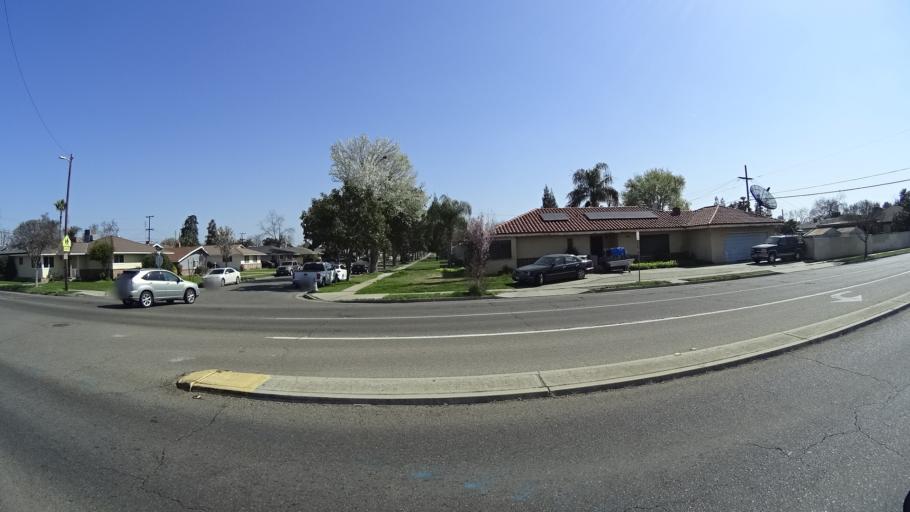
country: US
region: California
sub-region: Fresno County
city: Fresno
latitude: 36.7747
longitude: -119.8267
